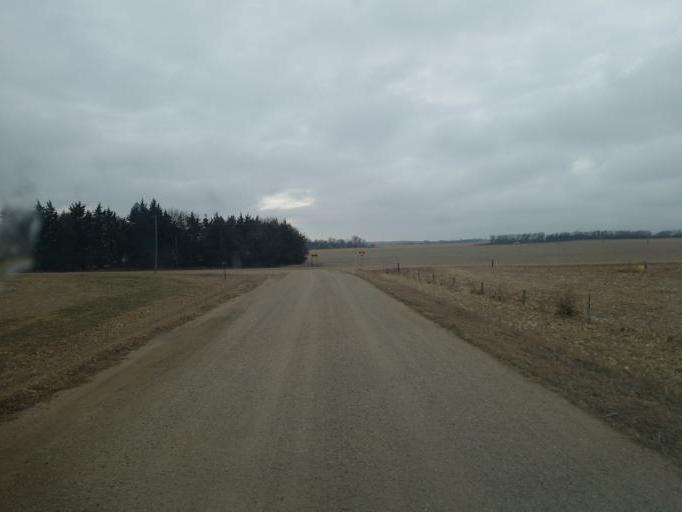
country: US
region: Nebraska
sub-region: Pierce County
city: Plainview
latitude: 42.4385
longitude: -97.7986
